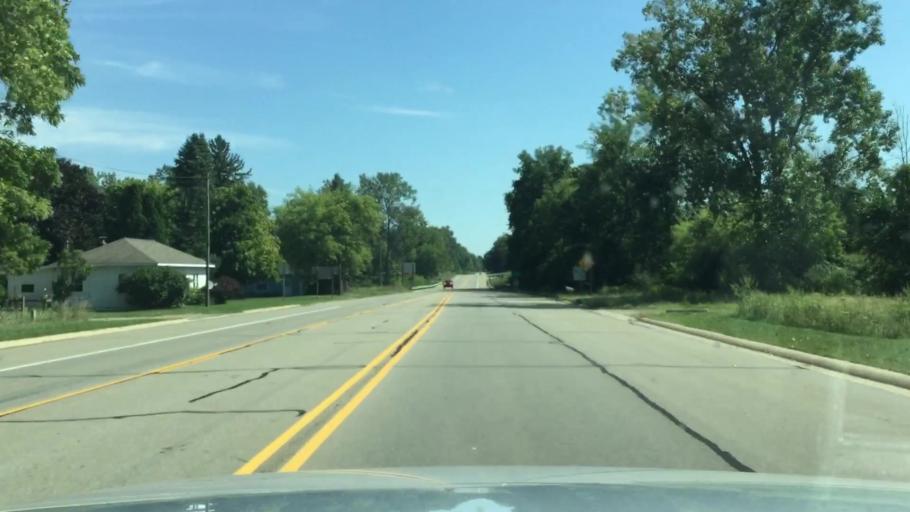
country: US
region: Michigan
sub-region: Jackson County
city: Brooklyn
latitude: 42.0593
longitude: -84.2194
